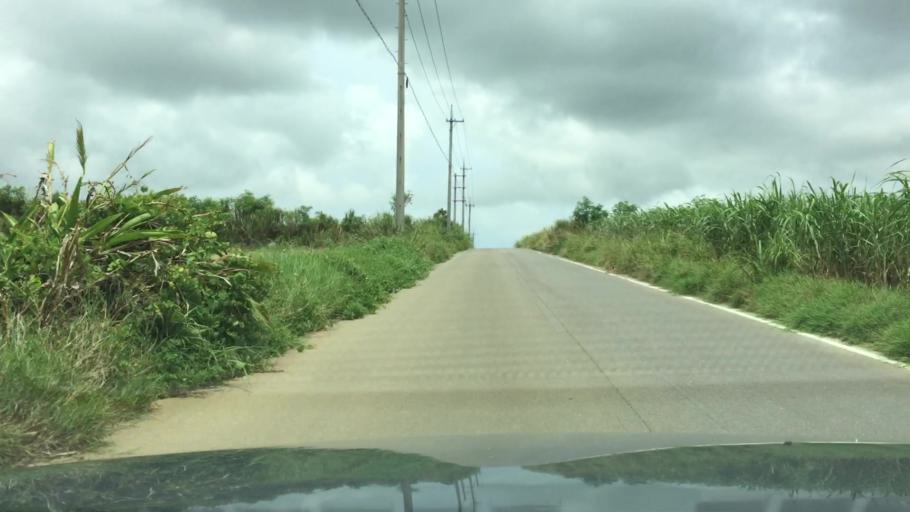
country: JP
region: Okinawa
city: Ishigaki
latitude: 24.3957
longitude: 124.1805
